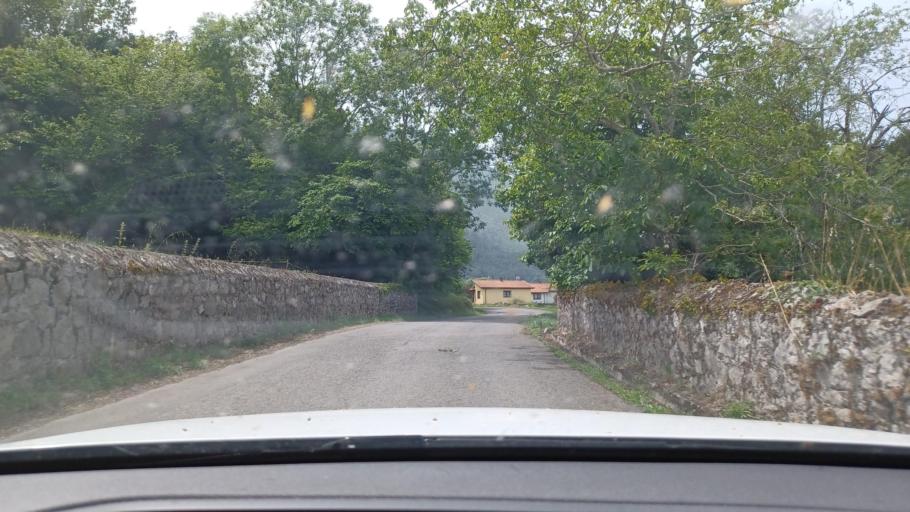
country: ES
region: Asturias
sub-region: Province of Asturias
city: Ribadesella
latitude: 43.4442
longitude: -4.9826
